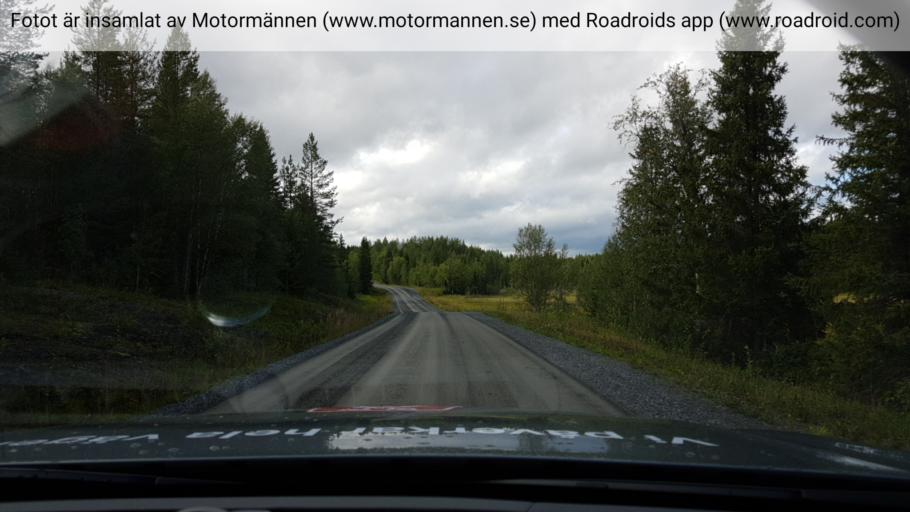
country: SE
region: Jaemtland
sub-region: Krokoms Kommun
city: Krokom
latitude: 63.7368
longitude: 14.4887
